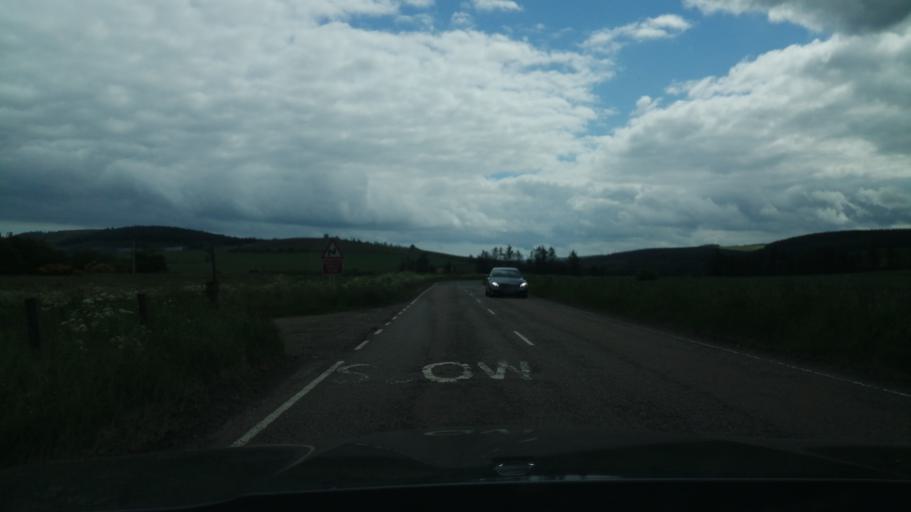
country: GB
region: Scotland
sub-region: Moray
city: Fochabers
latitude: 57.5453
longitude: -3.0896
